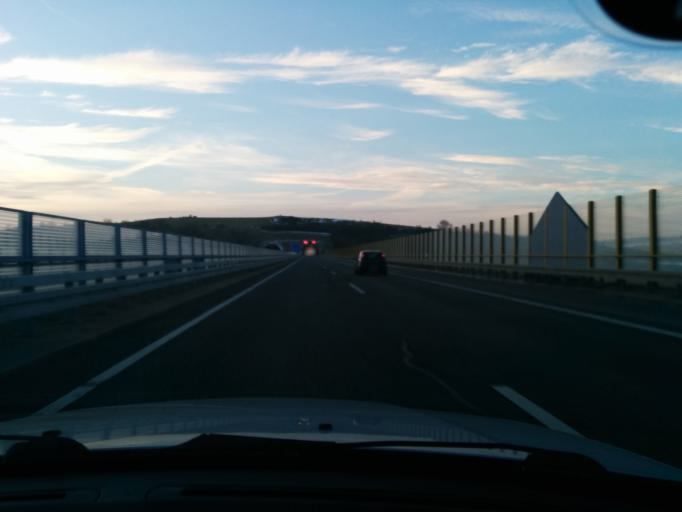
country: DE
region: Hesse
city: Hessisch Lichtenau
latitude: 51.1951
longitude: 9.7631
